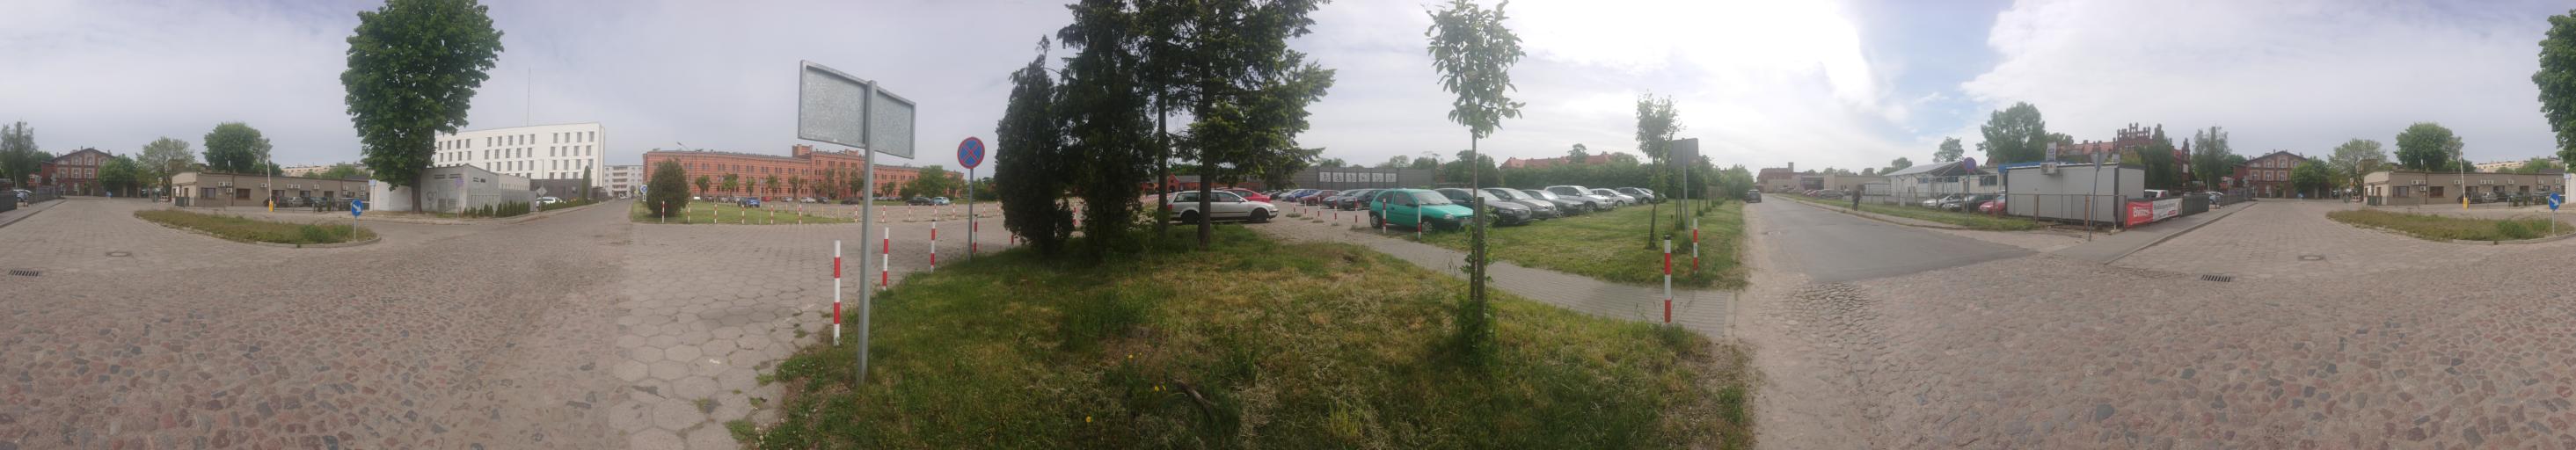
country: PL
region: Greater Poland Voivodeship
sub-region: Powiat gnieznienski
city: Gniezno
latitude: 52.5329
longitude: 17.6057
